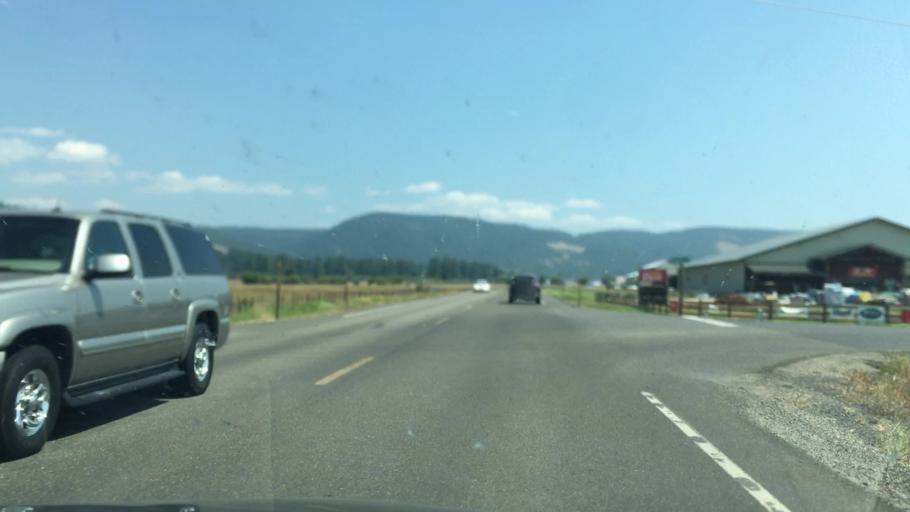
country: US
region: Idaho
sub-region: Valley County
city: McCall
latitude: 44.9679
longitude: -116.2702
